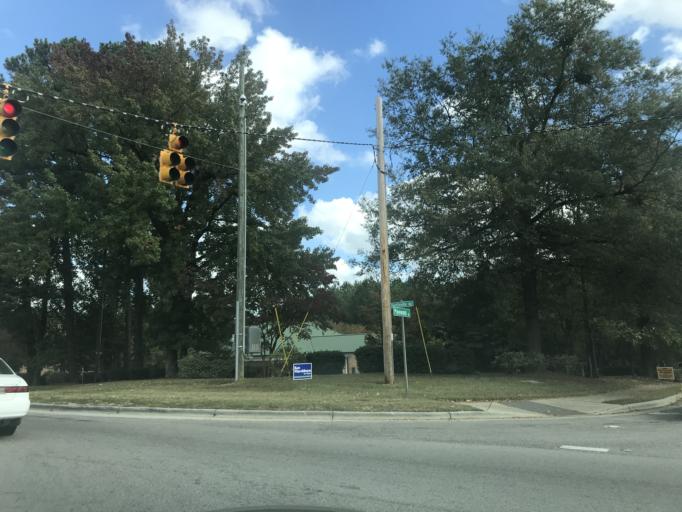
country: US
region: North Carolina
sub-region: Wake County
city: Garner
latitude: 35.7170
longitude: -78.6554
